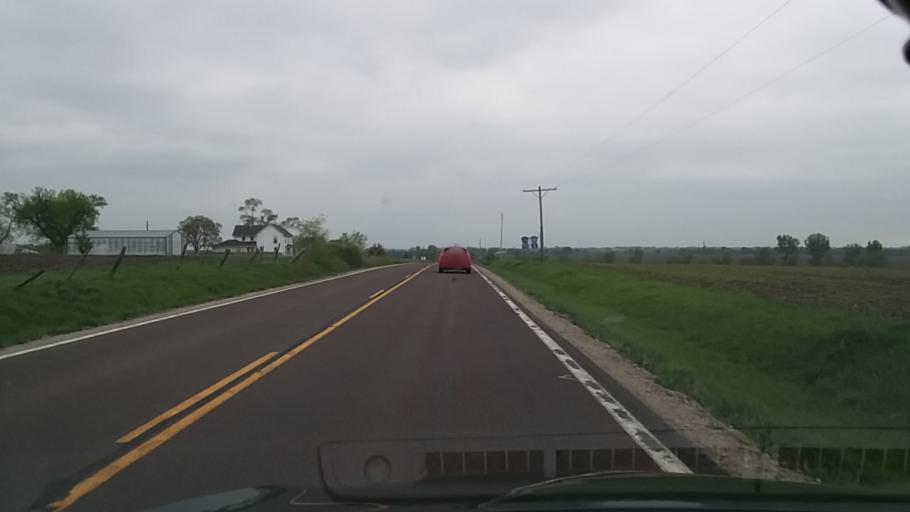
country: US
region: Kansas
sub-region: Douglas County
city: Eudora
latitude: 38.8714
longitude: -95.0933
